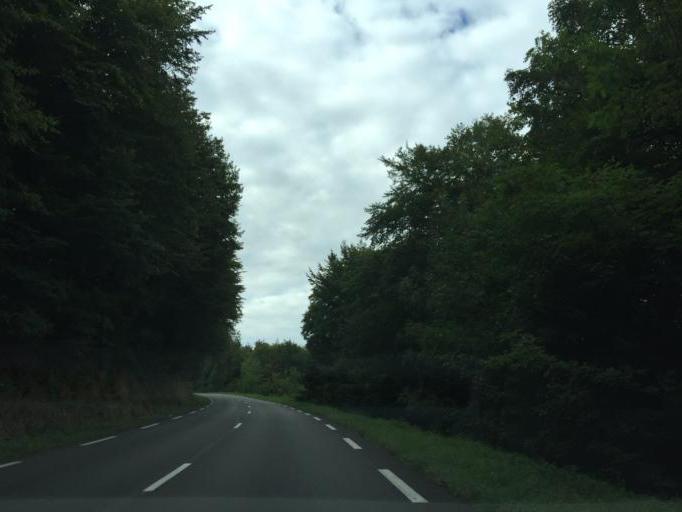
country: FR
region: Rhone-Alpes
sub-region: Departement de la Loire
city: Sorbiers
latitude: 45.4795
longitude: 4.4639
